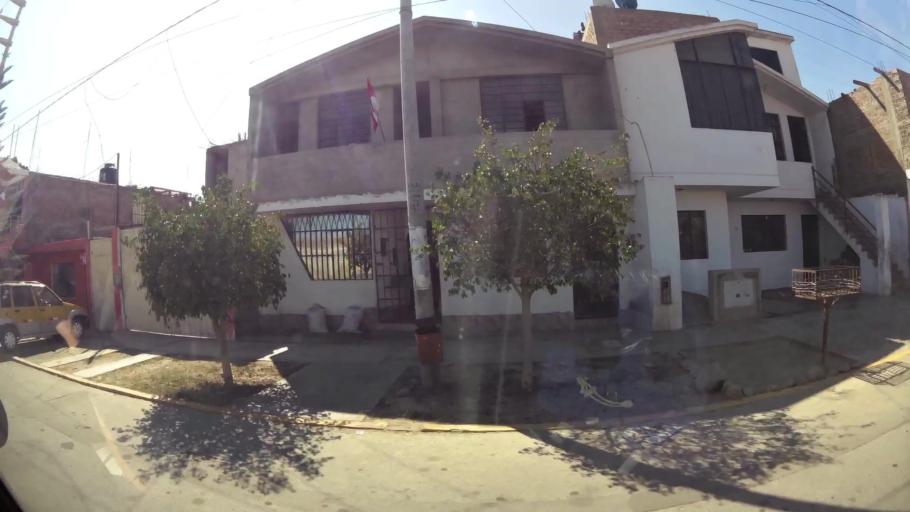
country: PE
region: Ica
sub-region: Provincia de Ica
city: La Tinguina
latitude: -14.0316
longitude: -75.7061
